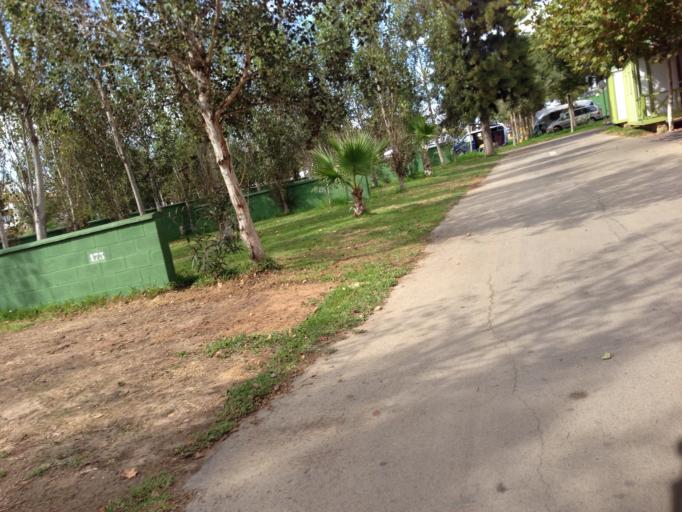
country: ES
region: Andalusia
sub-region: Provincia de Cadiz
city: Conil de la Frontera
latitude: 36.3121
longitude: -6.1133
